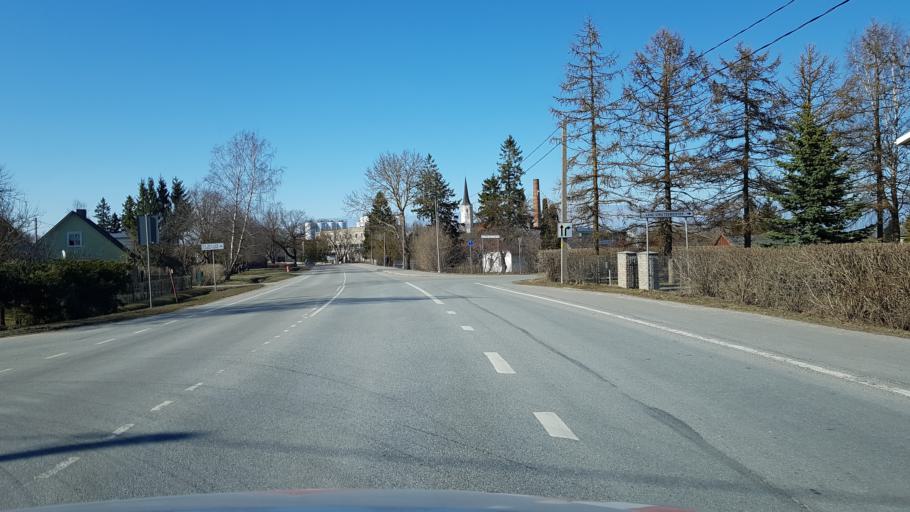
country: EE
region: Laeaene-Virumaa
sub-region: Haljala vald
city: Haljala
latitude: 59.4270
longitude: 26.2697
